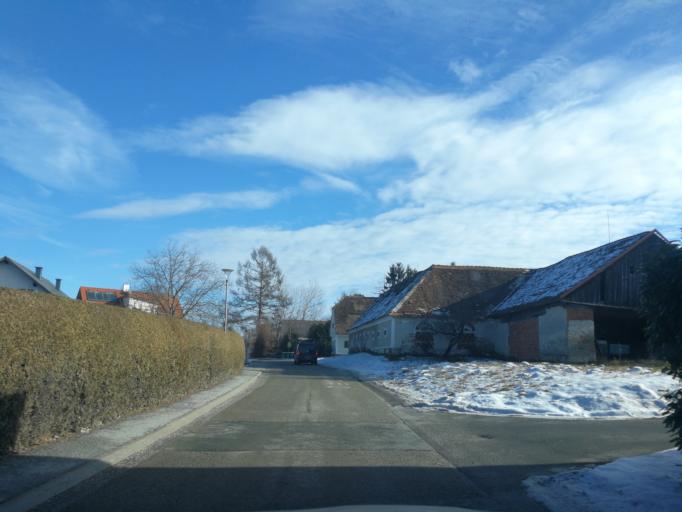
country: AT
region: Styria
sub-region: Politischer Bezirk Graz-Umgebung
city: Nestelbach bei Graz
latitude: 47.0972
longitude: 15.6169
